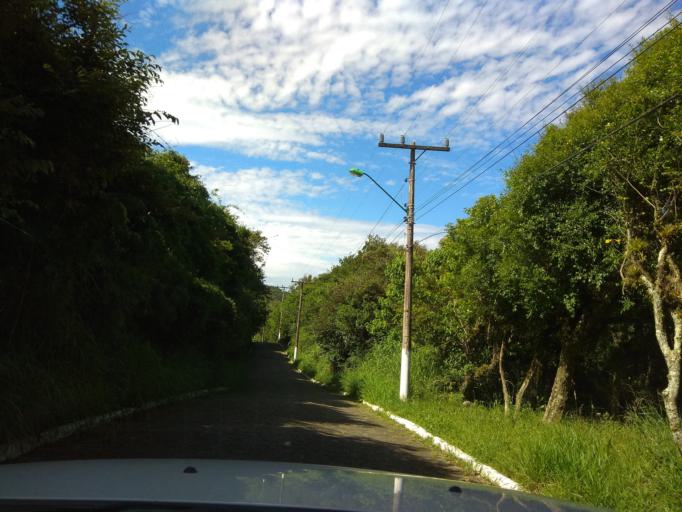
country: BR
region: Santa Catarina
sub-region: Laguna
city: Laguna
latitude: -28.4848
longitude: -48.7755
